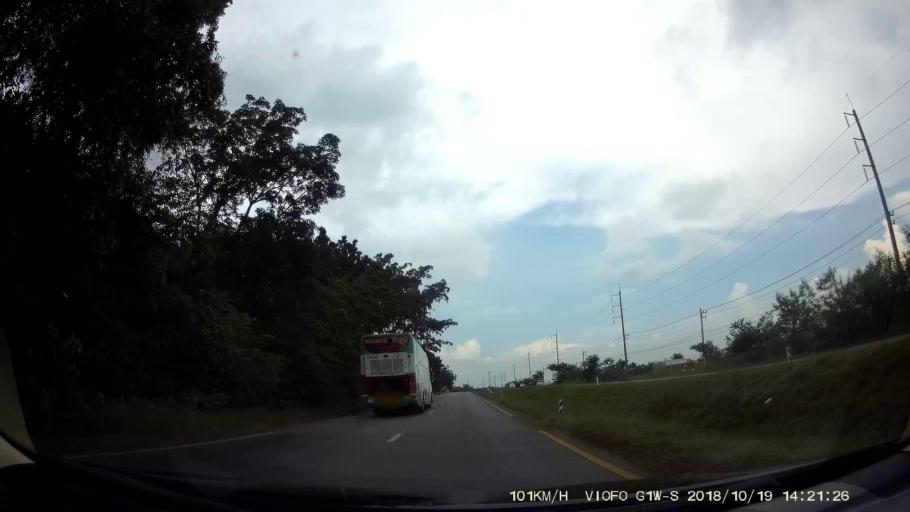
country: TH
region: Chaiyaphum
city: Kaeng Khro
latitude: 16.0521
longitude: 102.2664
